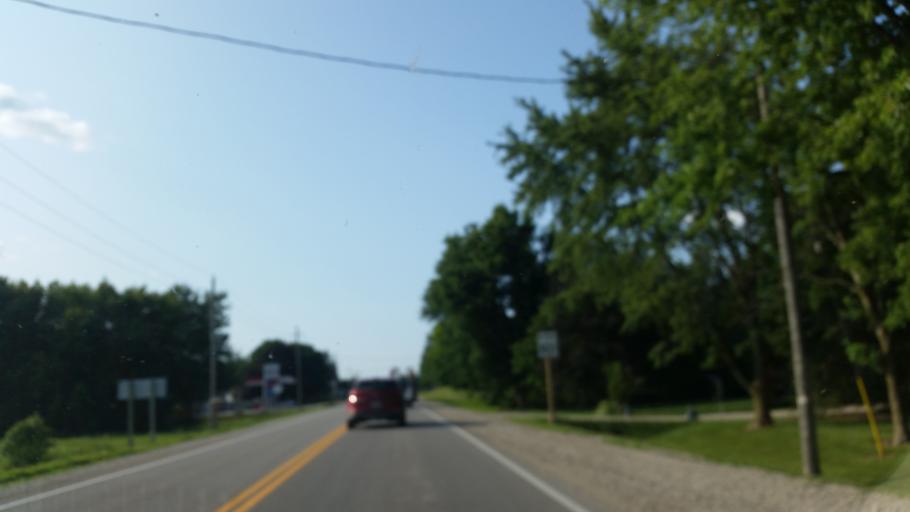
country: CA
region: Ontario
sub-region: Oxford County
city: Woodstock
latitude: 43.0025
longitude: -80.6031
